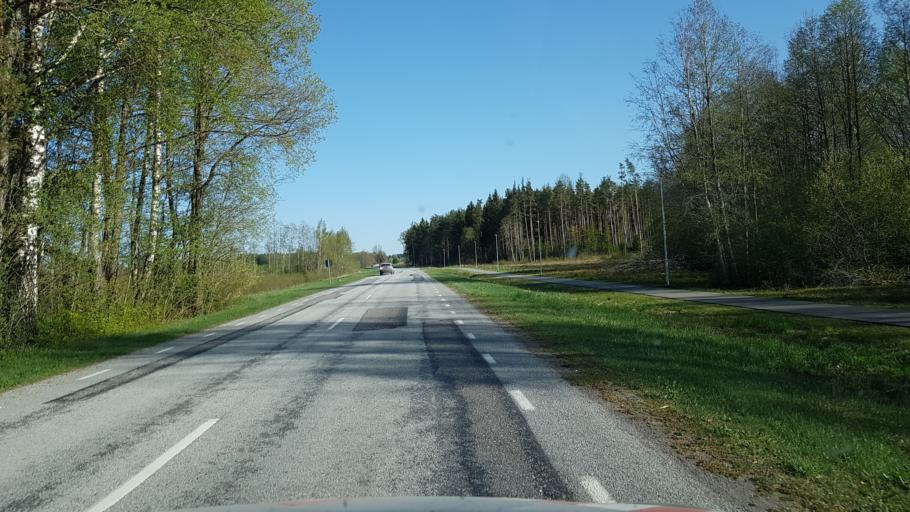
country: EE
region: Paernumaa
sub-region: Paikuse vald
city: Paikuse
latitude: 58.3678
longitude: 24.6381
